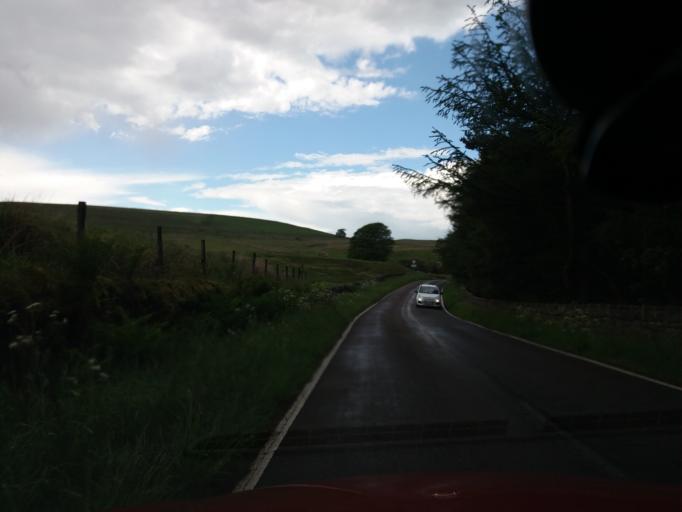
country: GB
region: England
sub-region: Blackburn with Darwen
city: Darwen
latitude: 53.6544
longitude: -2.4508
